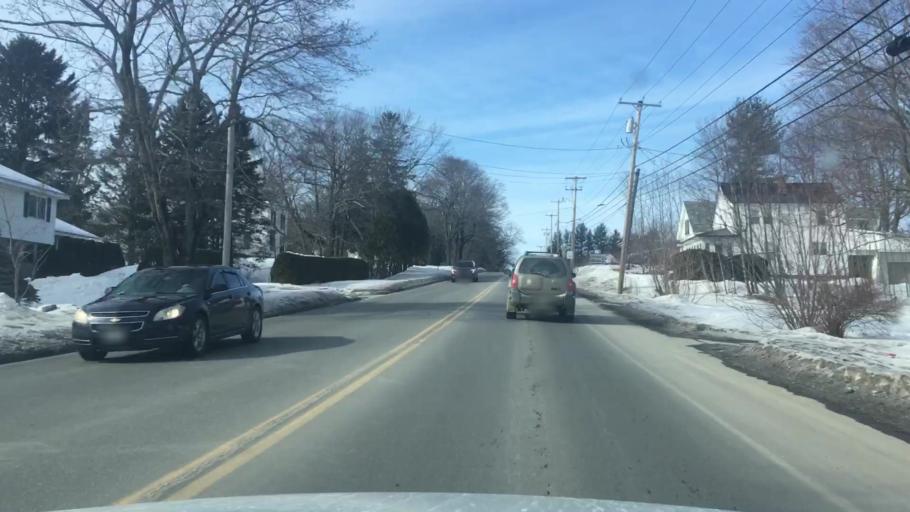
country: US
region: Maine
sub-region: Penobscot County
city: Bangor
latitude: 44.8278
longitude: -68.7833
